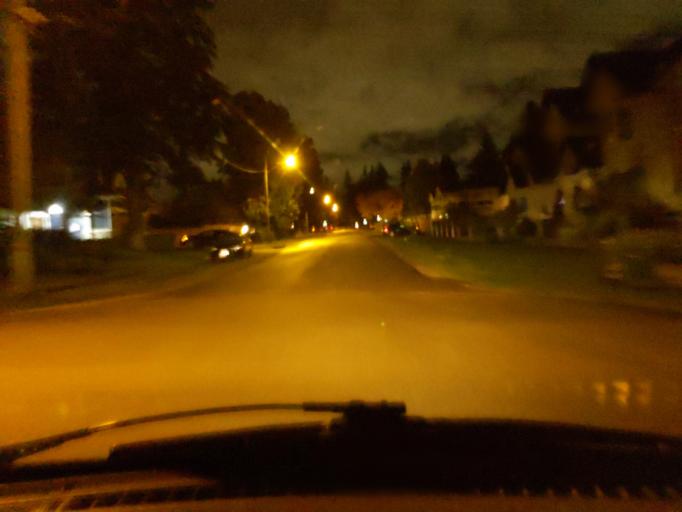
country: CA
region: British Columbia
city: New Westminster
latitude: 49.1981
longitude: -122.8646
